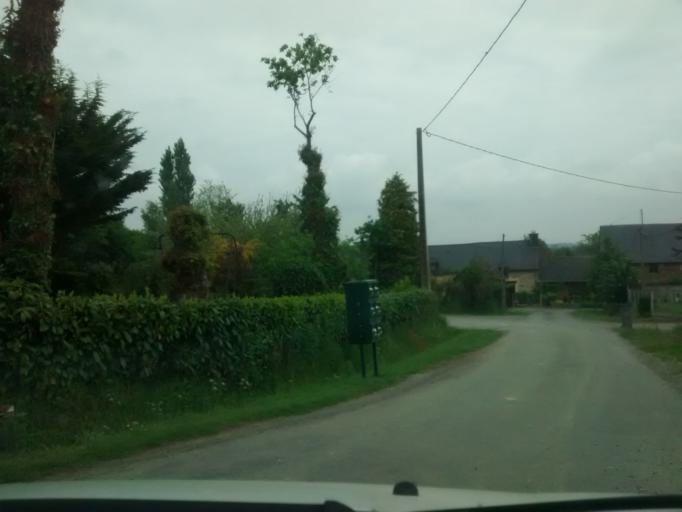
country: FR
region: Brittany
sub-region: Departement d'Ille-et-Vilaine
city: Fouillard
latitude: 48.1303
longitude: -1.5731
